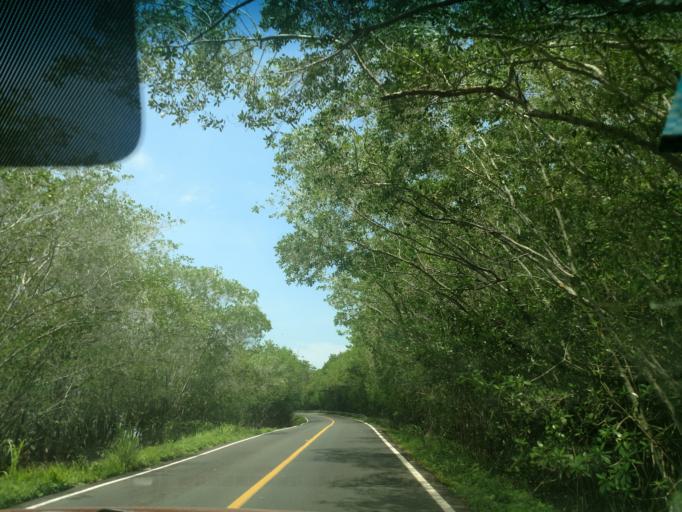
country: MX
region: Nayarit
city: San Blas
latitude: 21.5505
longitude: -105.2559
